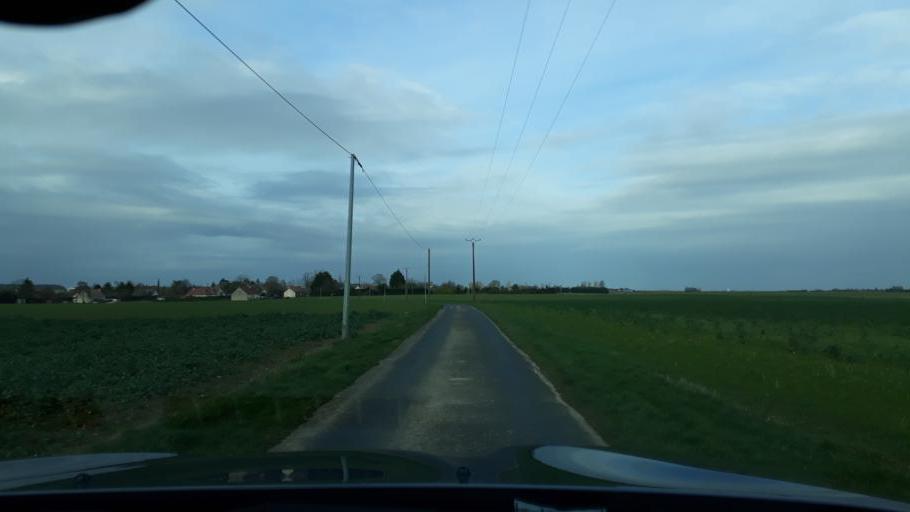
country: FR
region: Centre
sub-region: Departement du Loir-et-Cher
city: Mer
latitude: 47.7957
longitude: 1.4873
